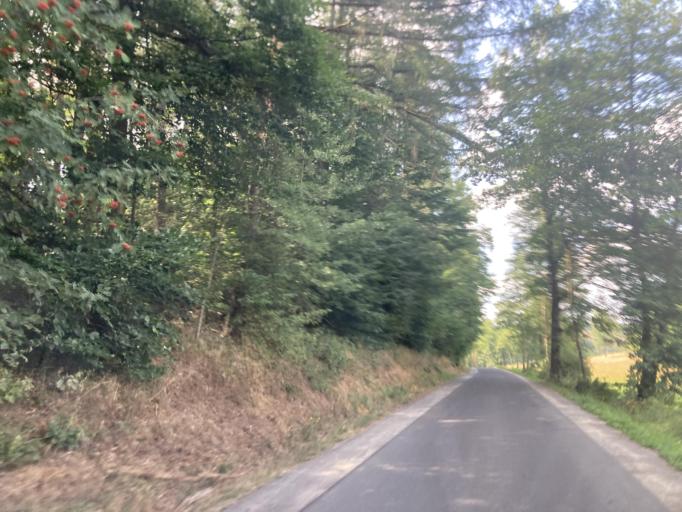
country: DE
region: Hesse
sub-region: Regierungsbezirk Kassel
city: Hosenfeld
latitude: 50.5358
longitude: 9.5240
